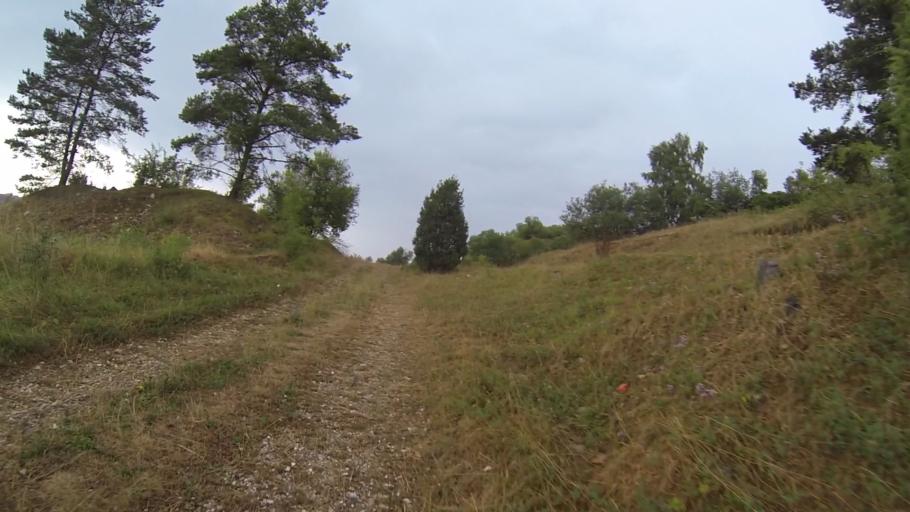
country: DE
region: Baden-Wuerttemberg
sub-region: Regierungsbezirk Stuttgart
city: Heidenheim an der Brenz
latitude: 48.6978
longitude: 10.1775
